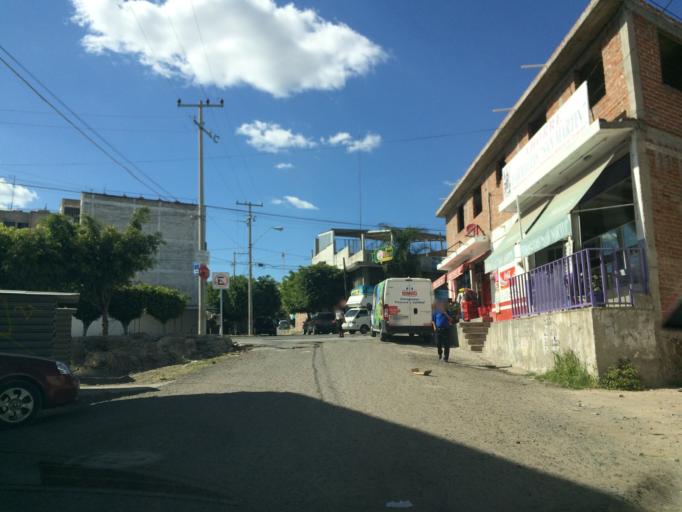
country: MX
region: Guanajuato
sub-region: Leon
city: Ejido la Joya
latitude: 21.1262
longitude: -101.7135
